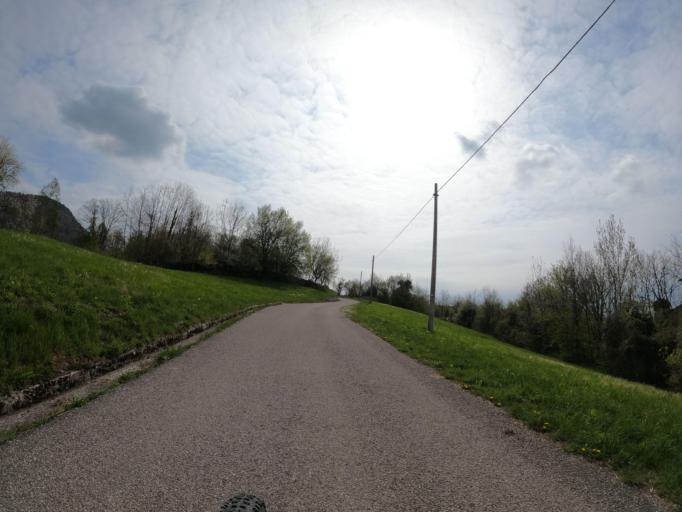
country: IT
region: Friuli Venezia Giulia
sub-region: Provincia di Udine
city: Clodig
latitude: 46.1443
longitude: 13.6124
